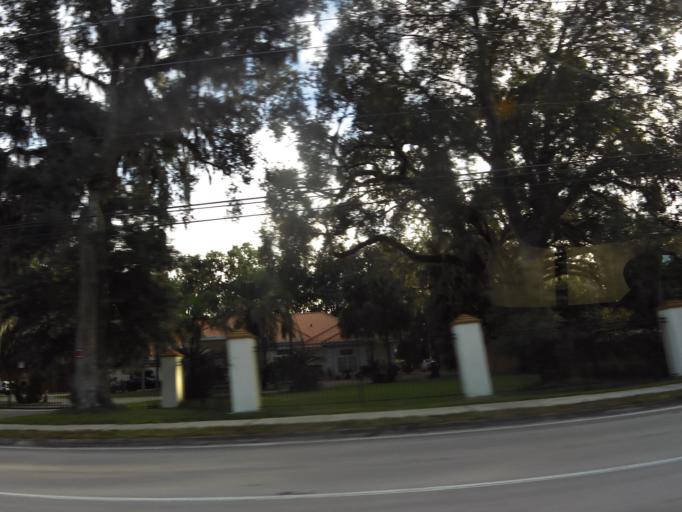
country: US
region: Florida
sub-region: Saint Johns County
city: Fruit Cove
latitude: 30.1602
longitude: -81.5948
